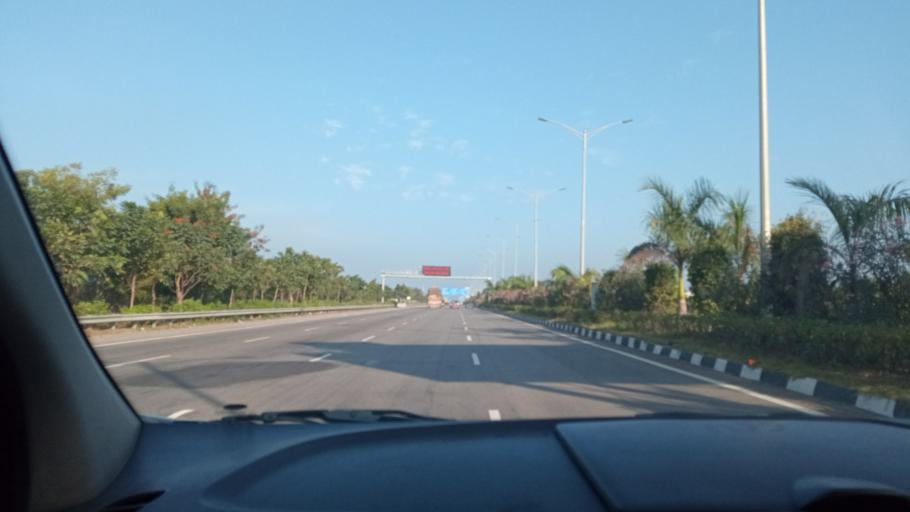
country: IN
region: Telangana
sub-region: Hyderabad
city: Hyderabad
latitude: 17.3335
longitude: 78.3696
